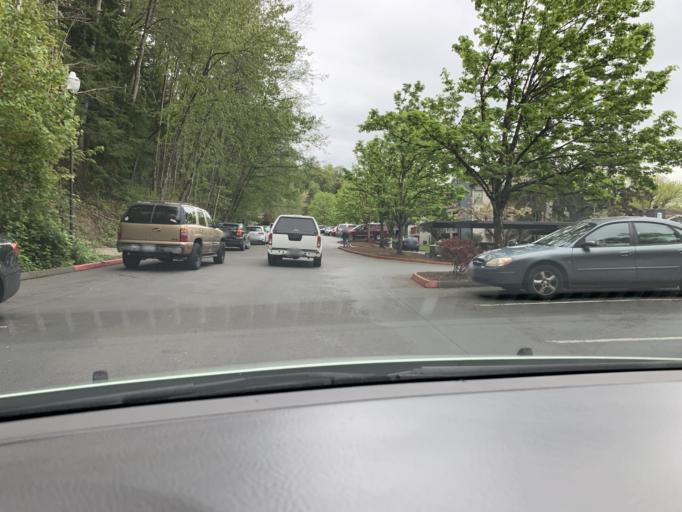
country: US
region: Washington
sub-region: King County
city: Kent
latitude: 47.3933
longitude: -122.2208
